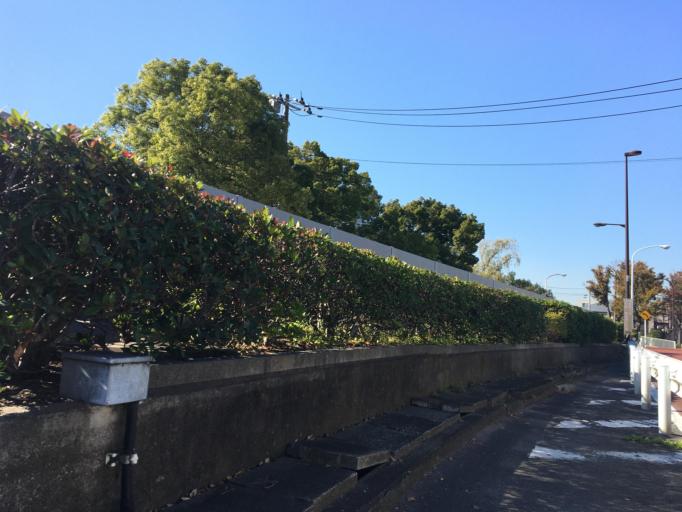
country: JP
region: Tokyo
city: Urayasu
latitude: 35.6836
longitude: 139.8964
